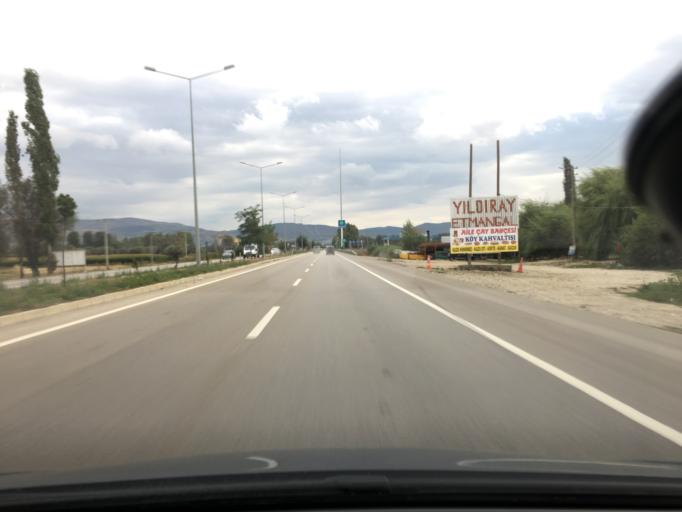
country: TR
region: Afyonkarahisar
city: Sincanli
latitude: 38.7627
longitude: 30.3645
